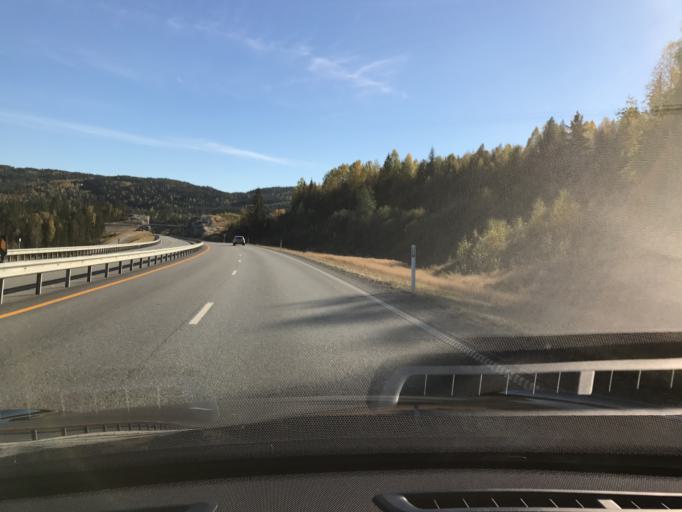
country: NO
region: Buskerud
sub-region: Krodsherad
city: Noresund
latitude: 60.2730
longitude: 9.7748
